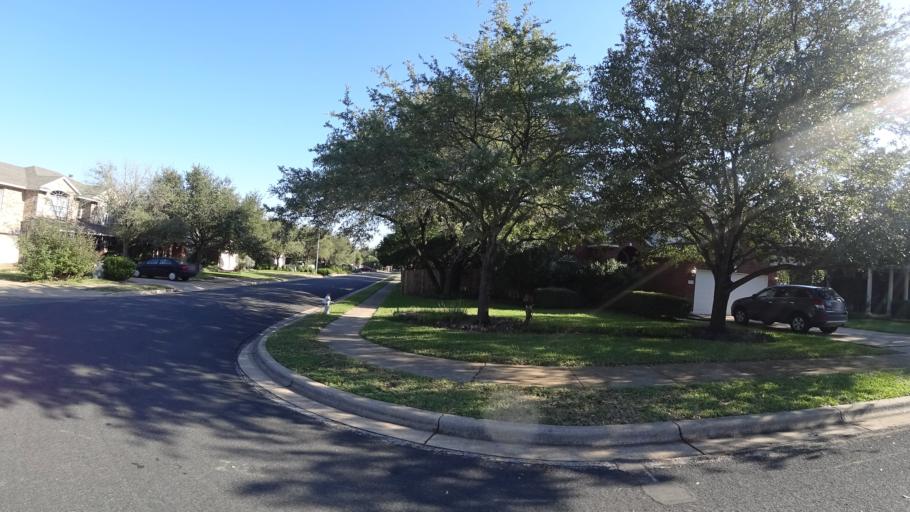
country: US
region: Texas
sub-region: Travis County
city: Shady Hollow
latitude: 30.2042
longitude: -97.8568
